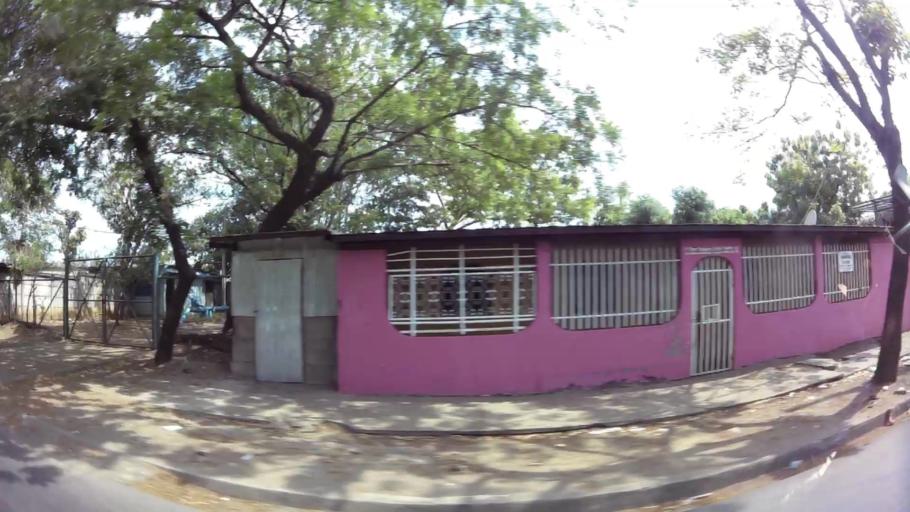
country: NI
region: Managua
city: Managua
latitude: 12.1506
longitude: -86.2698
